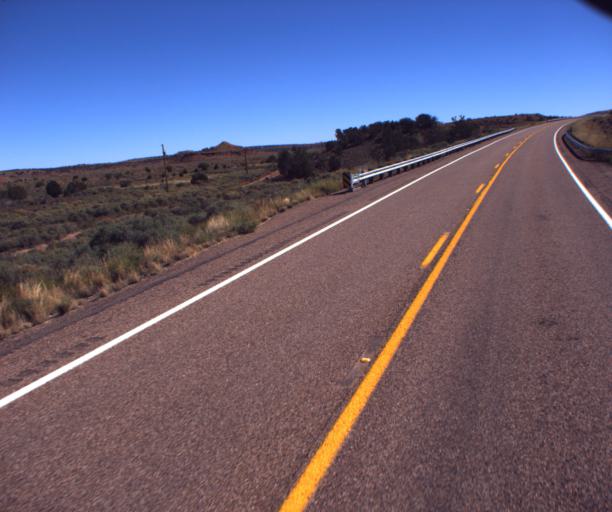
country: US
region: Arizona
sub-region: Apache County
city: Saint Johns
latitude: 34.5875
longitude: -109.5528
